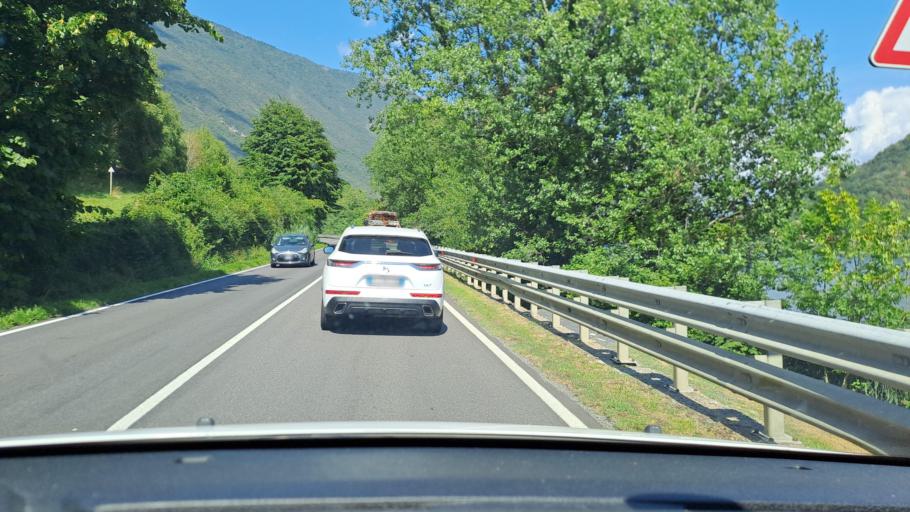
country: IT
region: Lombardy
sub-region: Provincia di Bergamo
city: Ranzanico
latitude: 45.7811
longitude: 9.9360
